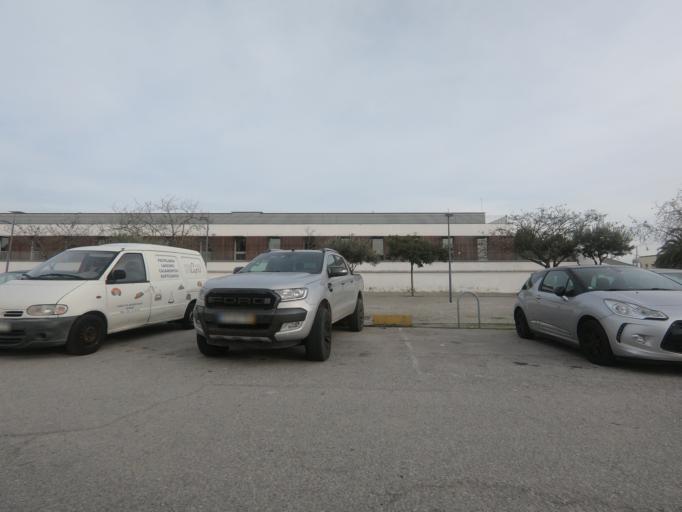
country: PT
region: Setubal
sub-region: Setubal
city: Setubal
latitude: 38.5219
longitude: -8.8889
